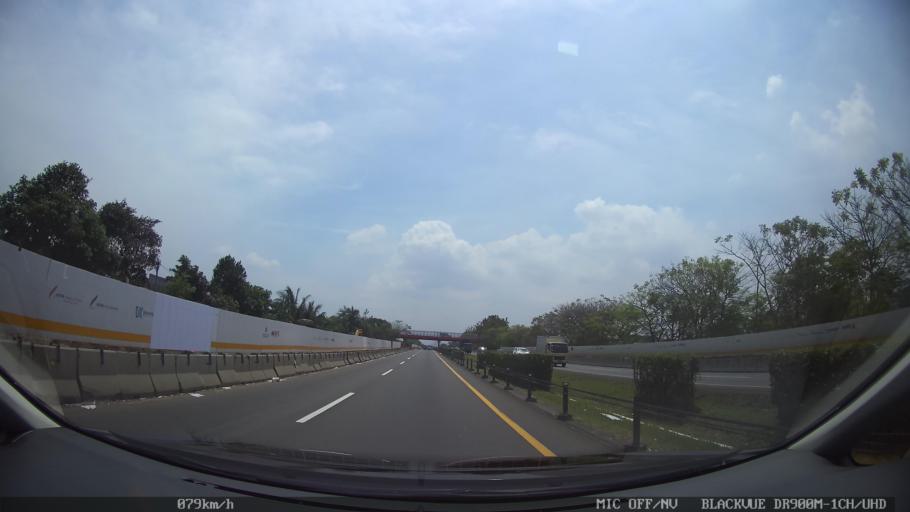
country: ID
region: Banten
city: Serang
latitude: -6.1386
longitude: 106.2324
